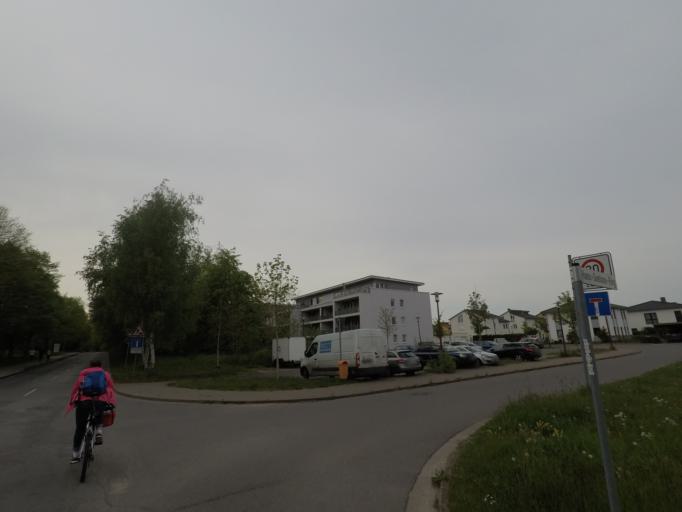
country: DE
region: Mecklenburg-Vorpommern
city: Rostock
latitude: 54.0661
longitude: 12.1277
